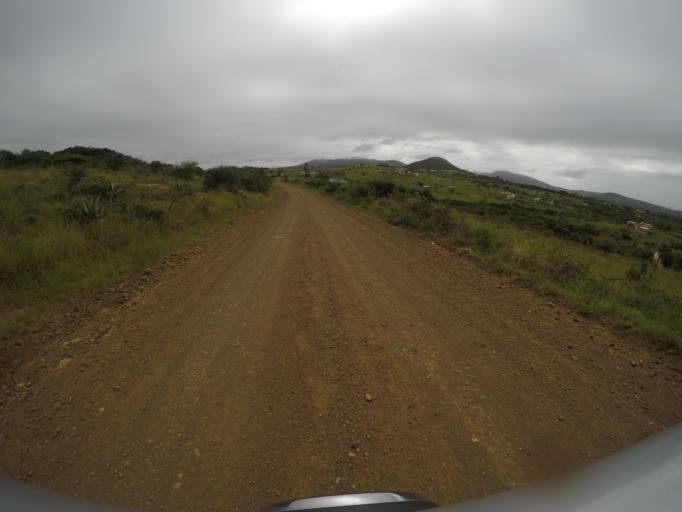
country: ZA
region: KwaZulu-Natal
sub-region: uThungulu District Municipality
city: Empangeni
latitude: -28.6057
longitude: 31.8367
